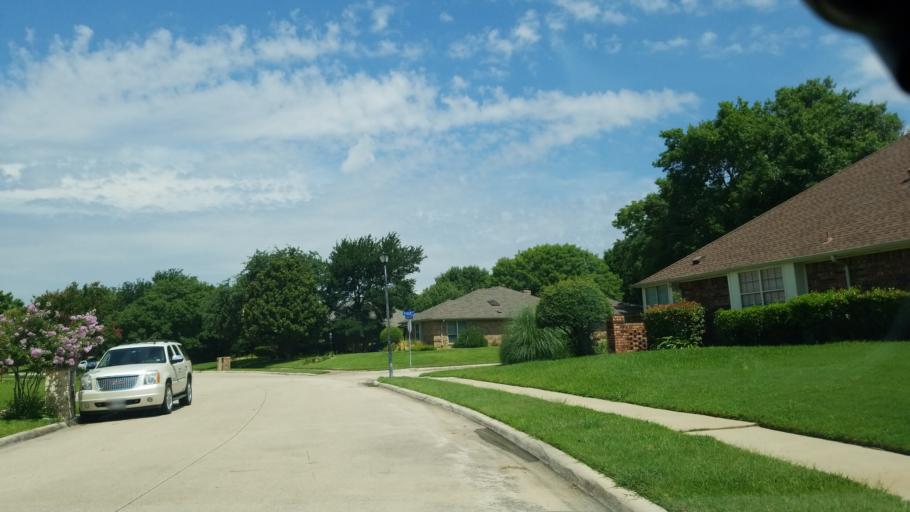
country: US
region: Texas
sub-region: Dallas County
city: Coppell
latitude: 32.9647
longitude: -96.9740
